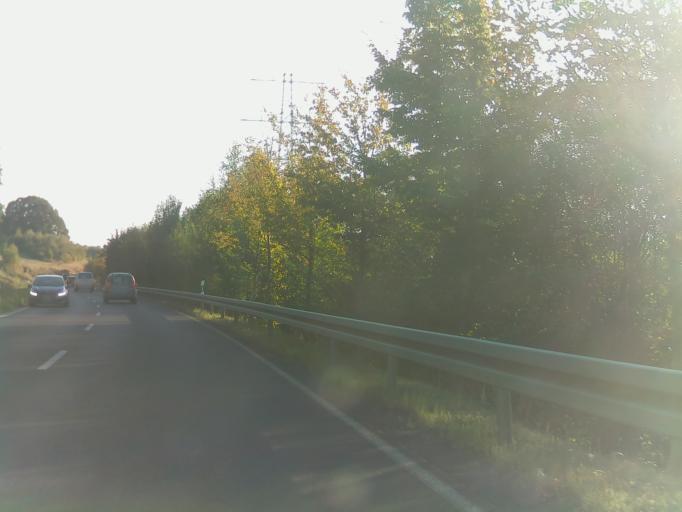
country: DE
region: Hesse
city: Hain-Grundau
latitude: 50.2436
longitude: 9.1522
